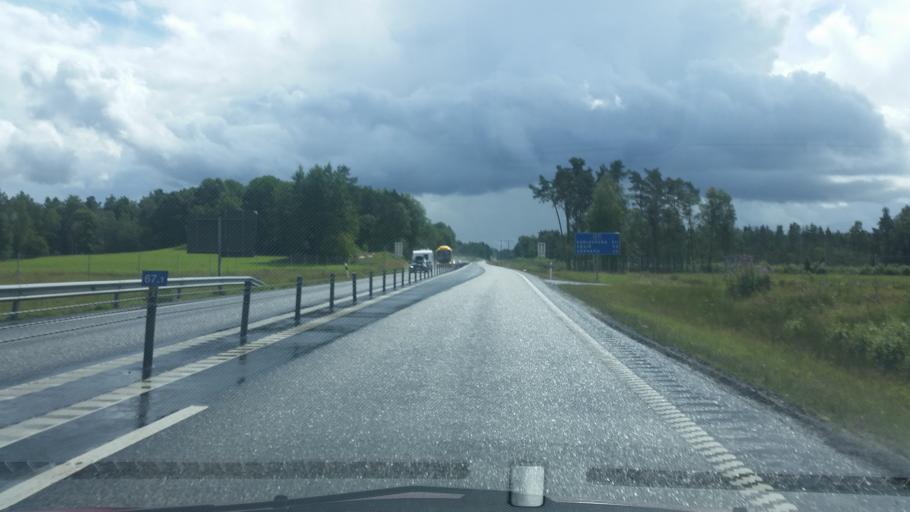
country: SE
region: Joenkoeping
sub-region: Gislaveds Kommun
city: Reftele
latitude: 57.2665
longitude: 13.6282
